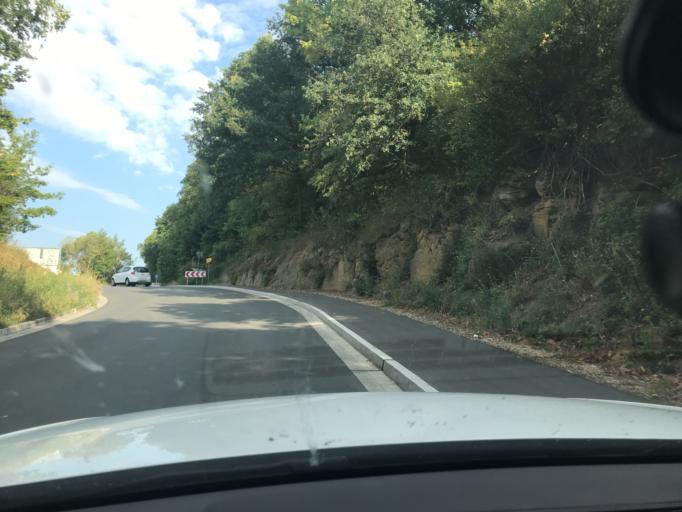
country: DE
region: Bavaria
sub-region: Upper Palatinate
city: Auerbach
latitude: 49.6975
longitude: 11.6187
